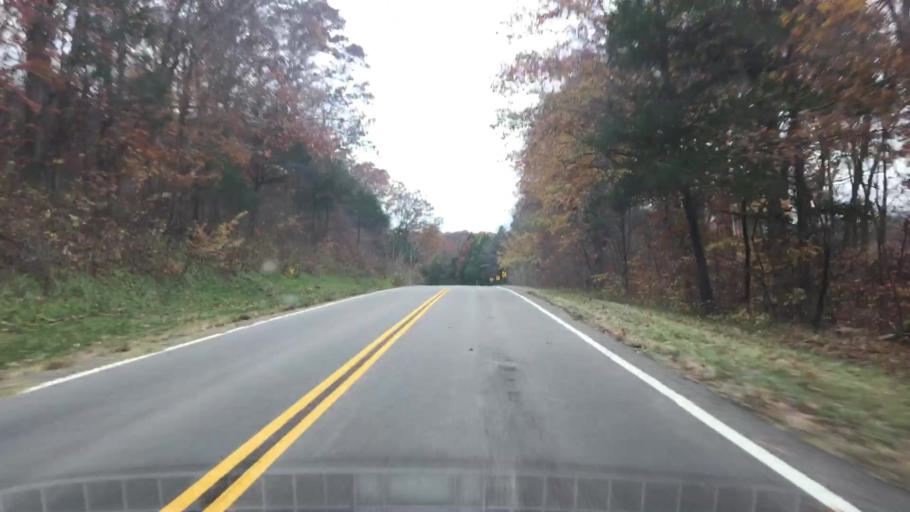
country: US
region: Missouri
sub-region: Gasconade County
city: Hermann
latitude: 38.7196
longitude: -91.6801
